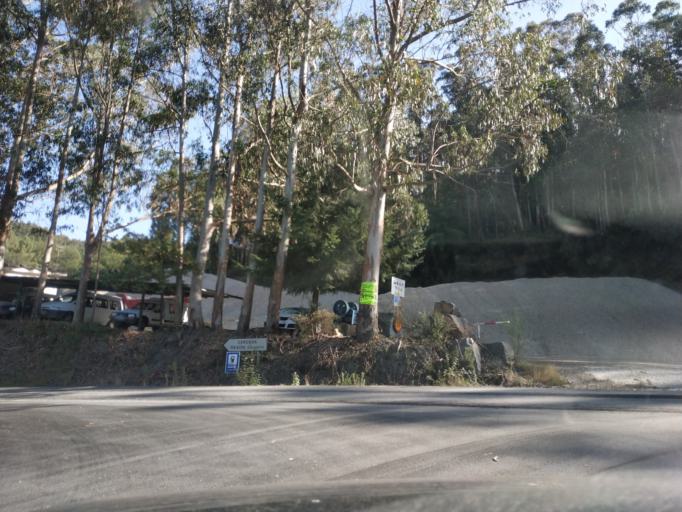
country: ES
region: Galicia
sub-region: Provincia da Coruna
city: Cerceda
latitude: 43.2323
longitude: -8.4647
